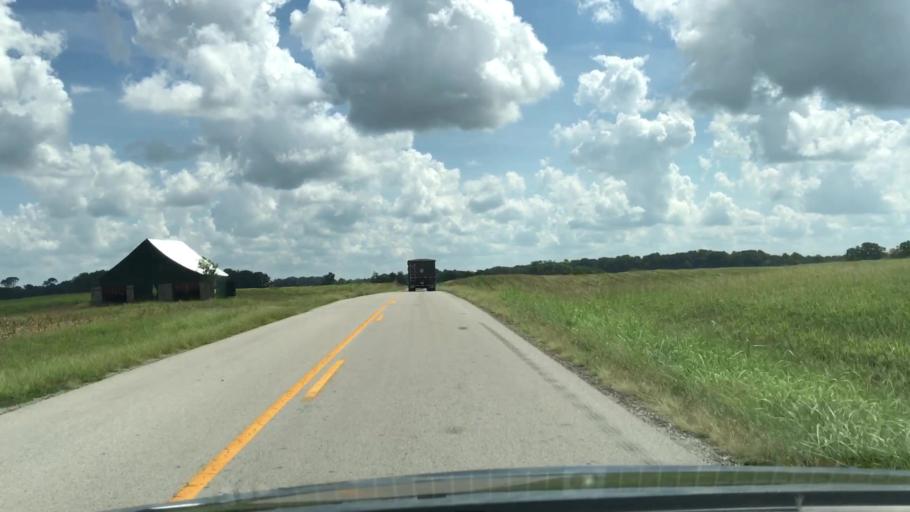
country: US
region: Kentucky
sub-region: Todd County
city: Guthrie
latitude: 36.6506
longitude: -87.0028
